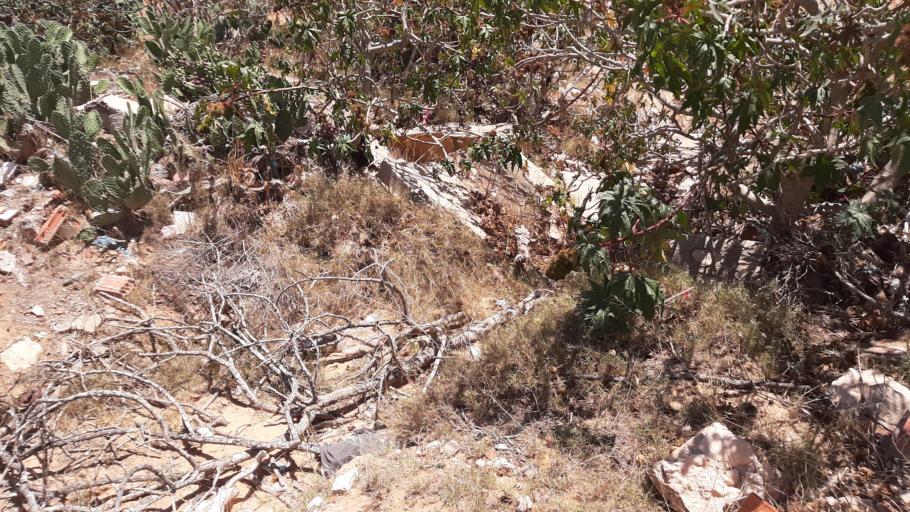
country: TN
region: Al Mahdiyah
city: El Jem
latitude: 35.0969
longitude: 10.6495
